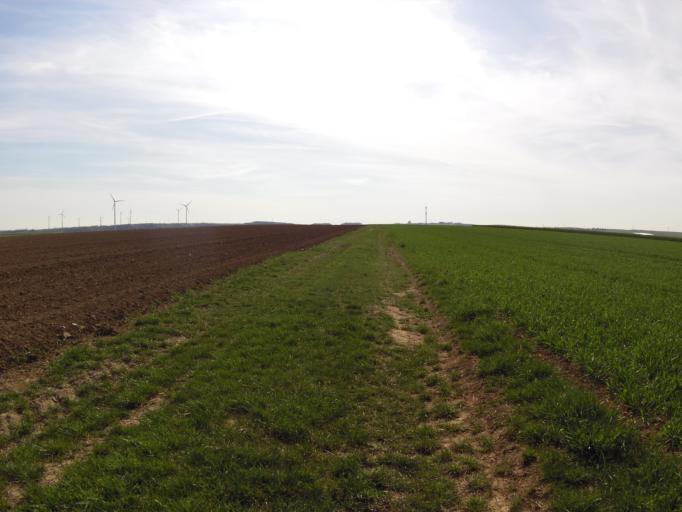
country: DE
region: Bavaria
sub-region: Regierungsbezirk Unterfranken
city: Mainstockheim
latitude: 49.7979
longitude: 10.1388
